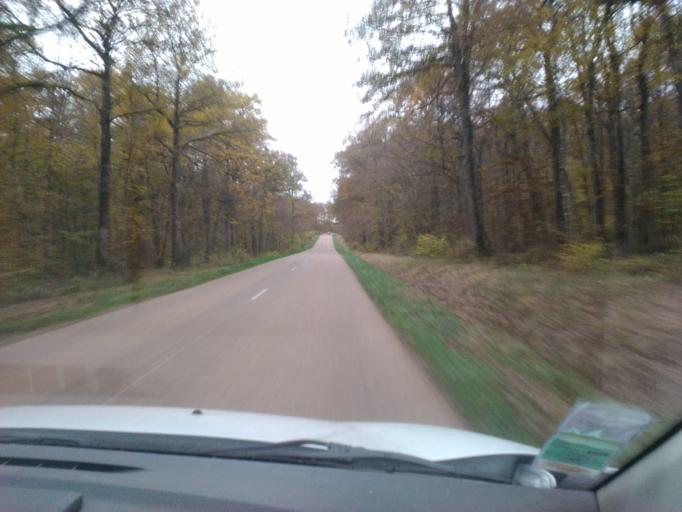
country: FR
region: Lorraine
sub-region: Departement des Vosges
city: Mirecourt
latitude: 48.2958
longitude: 6.2105
